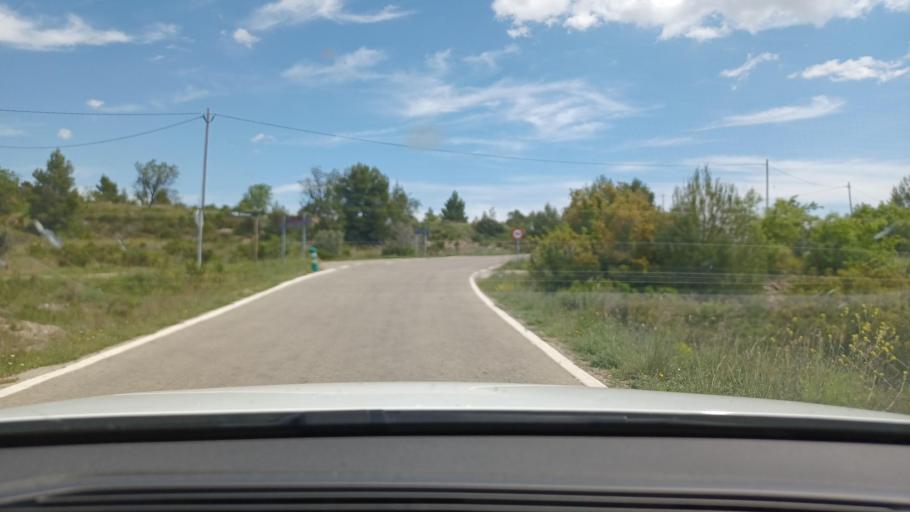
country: ES
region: Valencia
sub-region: Provincia de Castello
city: Rosell
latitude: 40.6454
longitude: 0.2710
